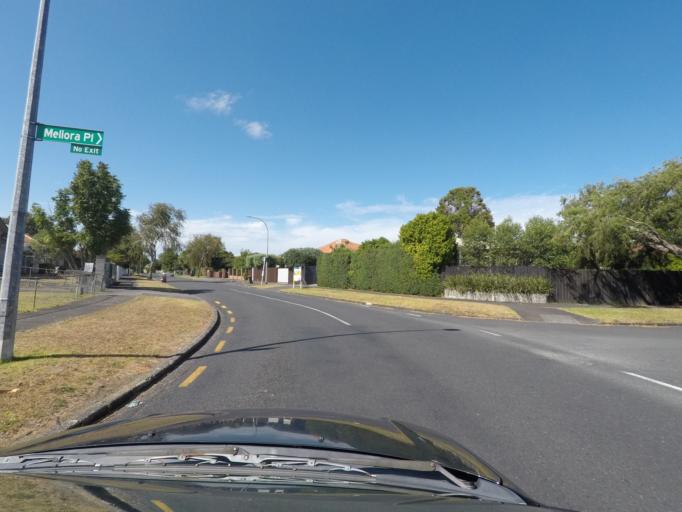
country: NZ
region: Auckland
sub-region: Auckland
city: Rosebank
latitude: -36.8875
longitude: 174.6776
